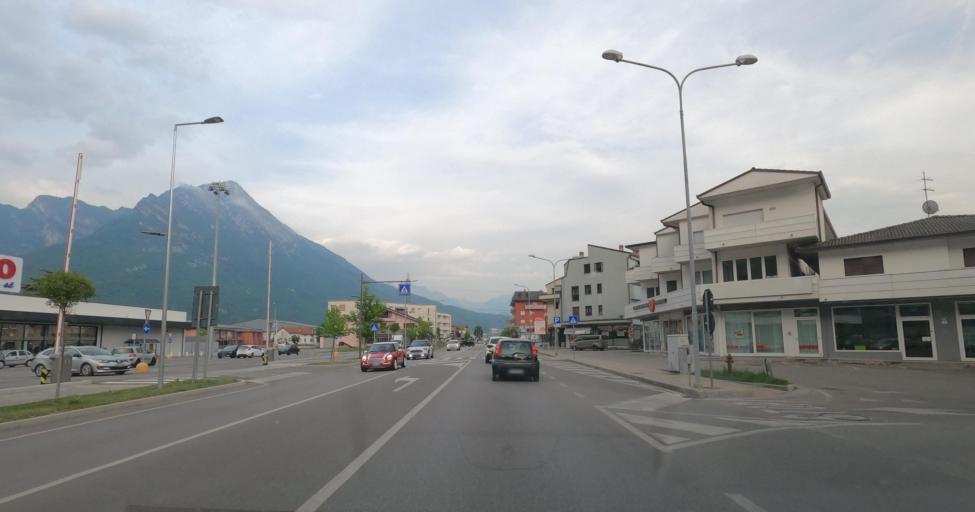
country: IT
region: Veneto
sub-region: Provincia di Belluno
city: Ponte nell'Alpi
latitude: 46.1807
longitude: 12.2771
